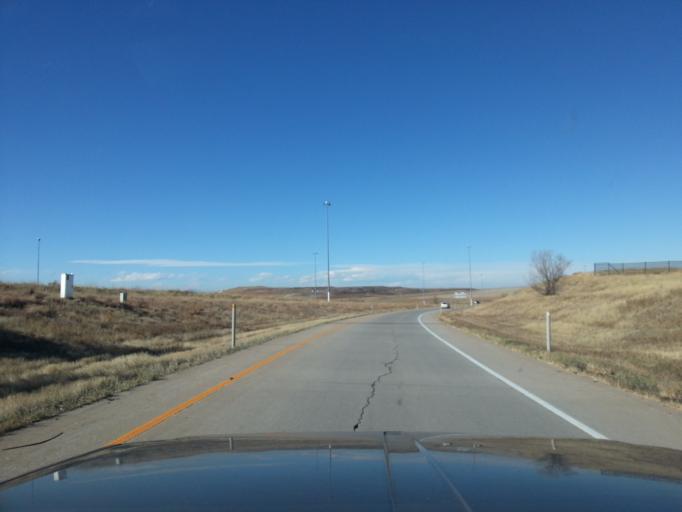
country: US
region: Colorado
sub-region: Adams County
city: Aurora
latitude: 39.8371
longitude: -104.7449
